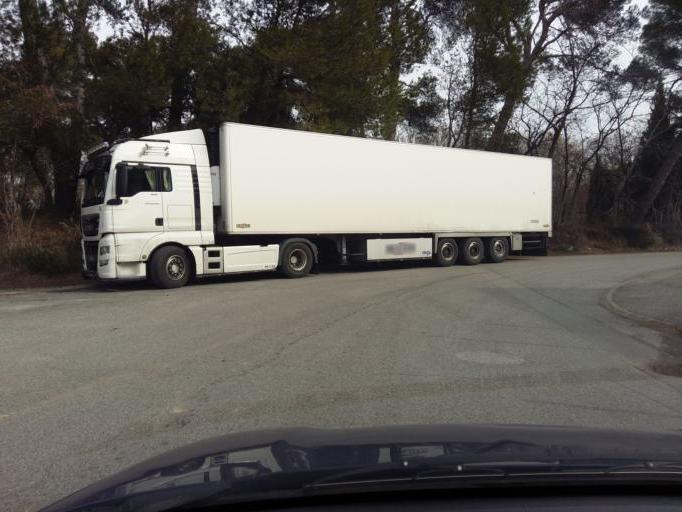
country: FR
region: Provence-Alpes-Cote d'Azur
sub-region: Departement des Bouches-du-Rhone
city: Noves
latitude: 43.8866
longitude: 4.8951
